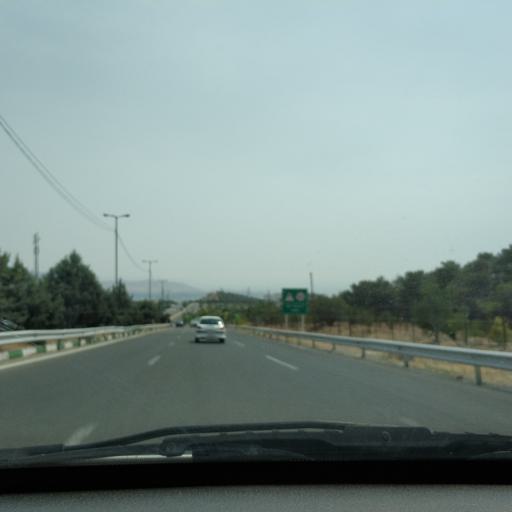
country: IR
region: Tehran
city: Tajrish
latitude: 35.7748
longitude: 51.5597
